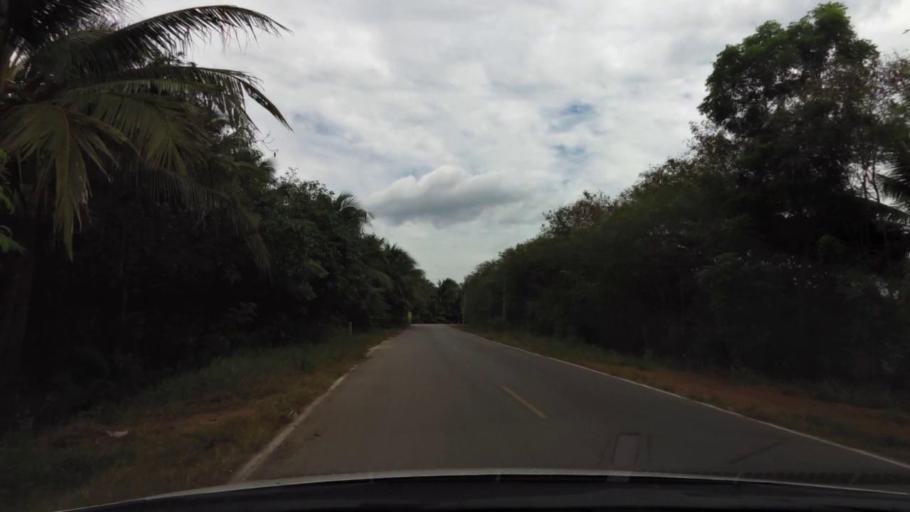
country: TH
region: Ratchaburi
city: Damnoen Saduak
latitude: 13.5567
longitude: 99.9757
